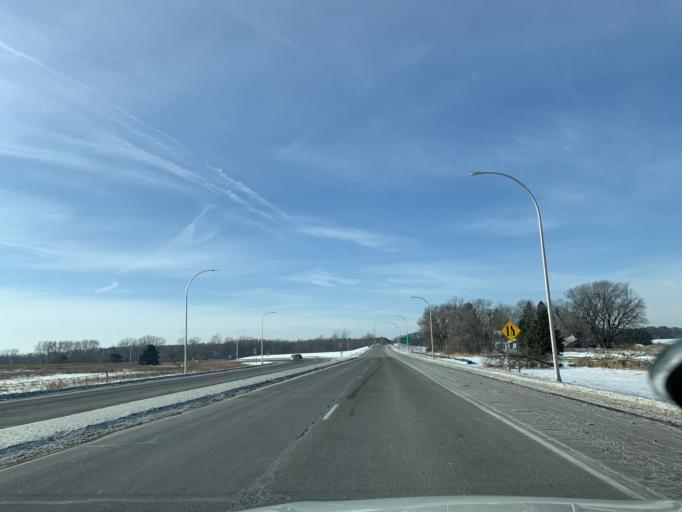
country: US
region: Minnesota
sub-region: Washington County
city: Forest Lake
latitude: 45.2899
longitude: -92.9978
